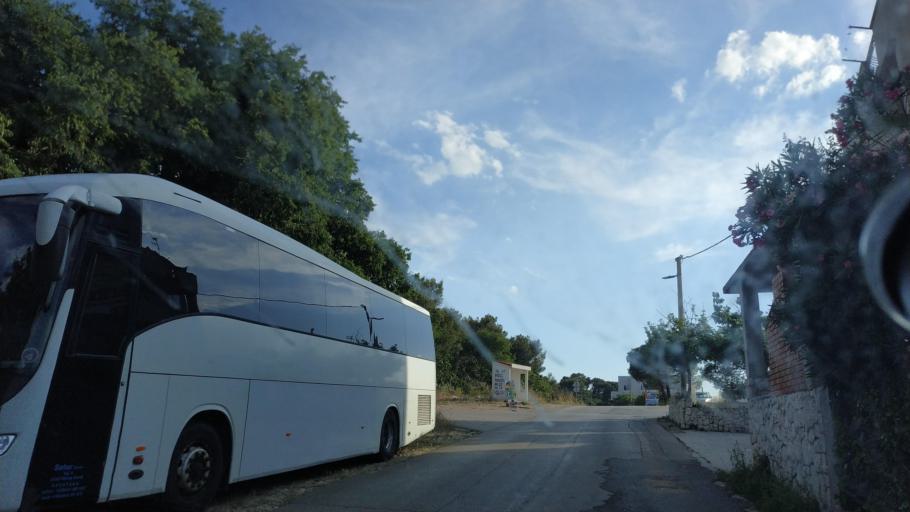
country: HR
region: Splitsko-Dalmatinska
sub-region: Grad Trogir
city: Trogir
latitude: 43.4902
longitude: 16.2543
